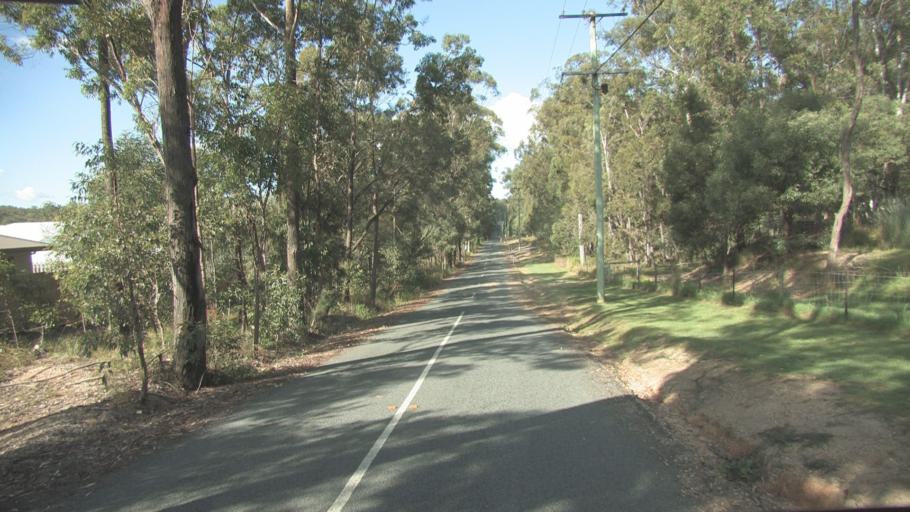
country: AU
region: Queensland
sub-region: Redland
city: Redland Bay
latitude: -27.6531
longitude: 153.2555
